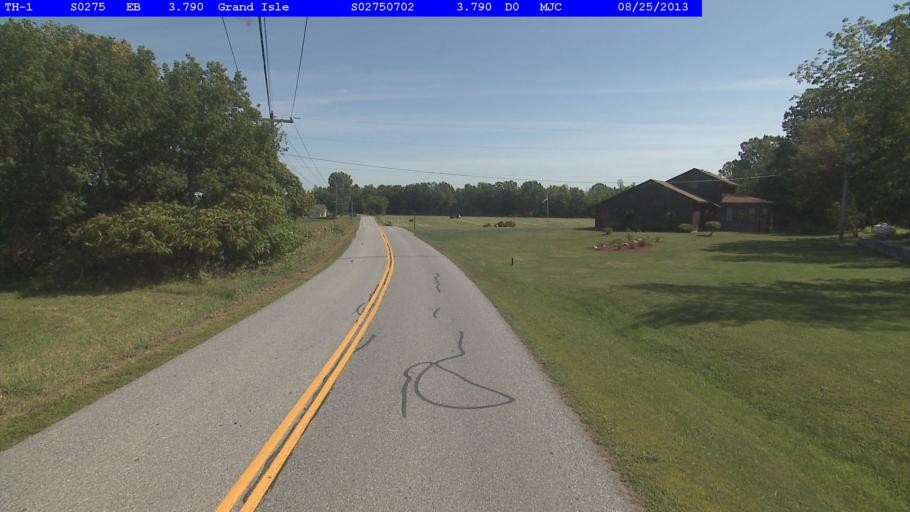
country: US
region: Vermont
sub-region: Grand Isle County
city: North Hero
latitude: 44.7363
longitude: -73.3053
